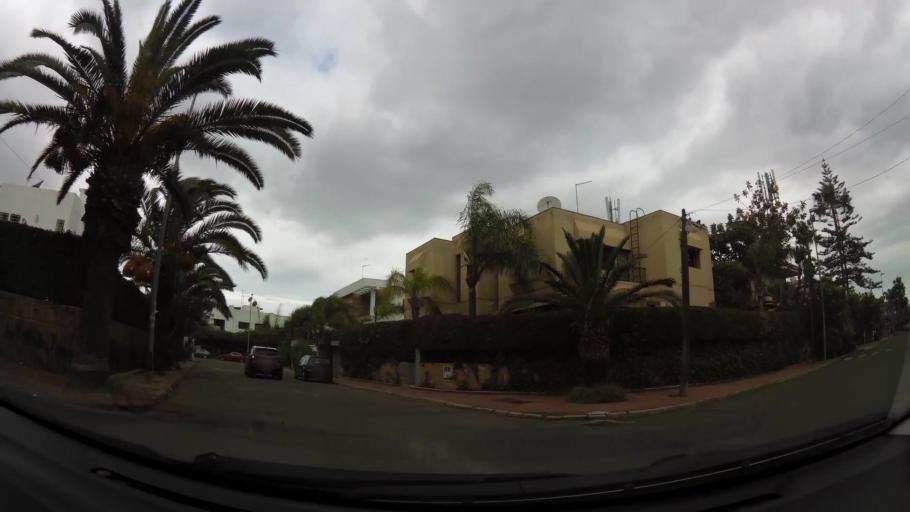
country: MA
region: Grand Casablanca
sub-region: Casablanca
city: Casablanca
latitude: 33.5686
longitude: -7.6585
